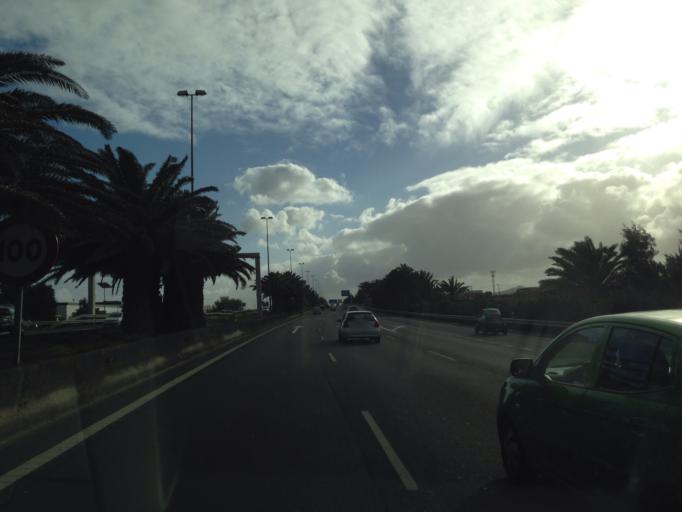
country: ES
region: Canary Islands
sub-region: Provincia de Las Palmas
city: Telde
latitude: 27.9471
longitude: -15.3879
